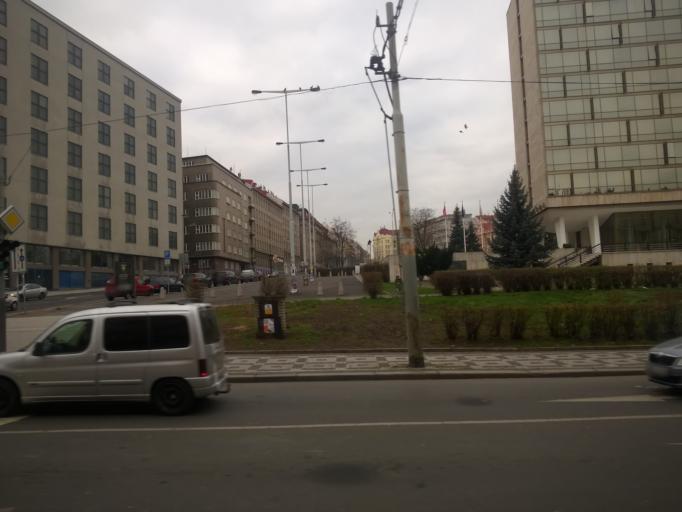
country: CZ
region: Praha
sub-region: Praha 8
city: Karlin
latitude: 50.1025
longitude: 14.4327
